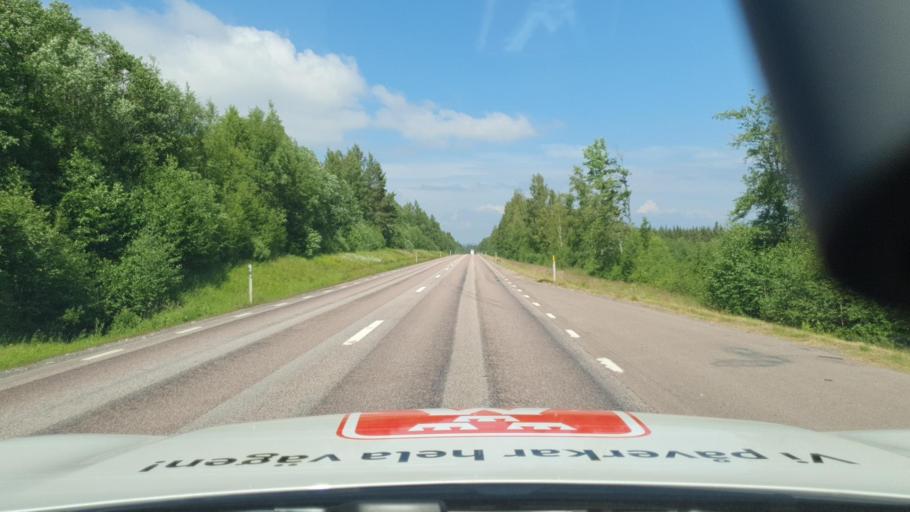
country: SE
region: Vaermland
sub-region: Torsby Kommun
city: Torsby
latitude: 60.0570
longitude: 13.0601
